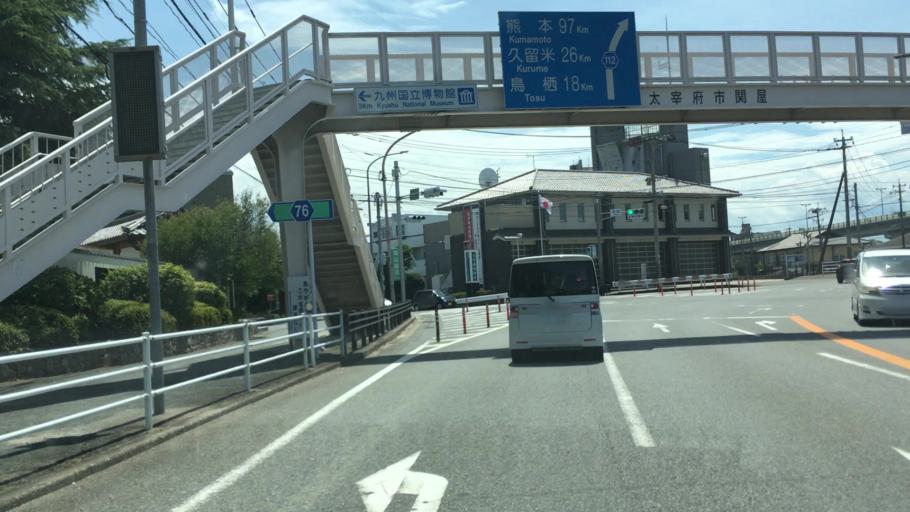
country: JP
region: Fukuoka
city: Dazaifu
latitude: 33.5135
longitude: 130.5079
